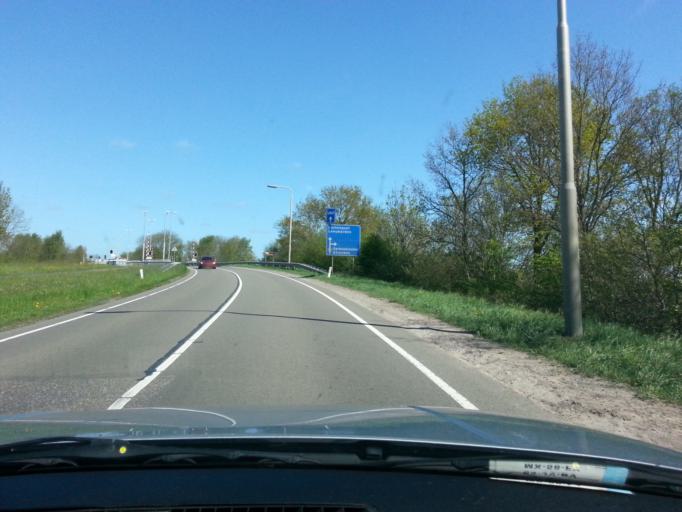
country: NL
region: Friesland
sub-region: Gemeente Achtkarspelen
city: Augustinusga
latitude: 53.2249
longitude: 6.1740
